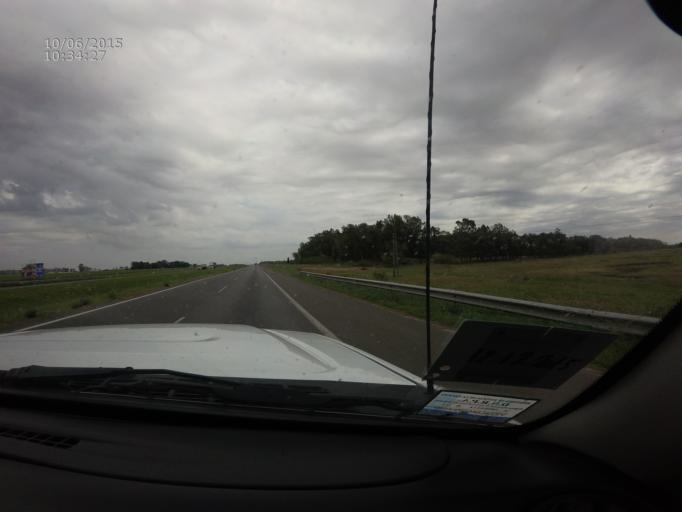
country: AR
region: Buenos Aires
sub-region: Partido de Ramallo
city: Ramallo
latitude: -33.5825
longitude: -60.0502
